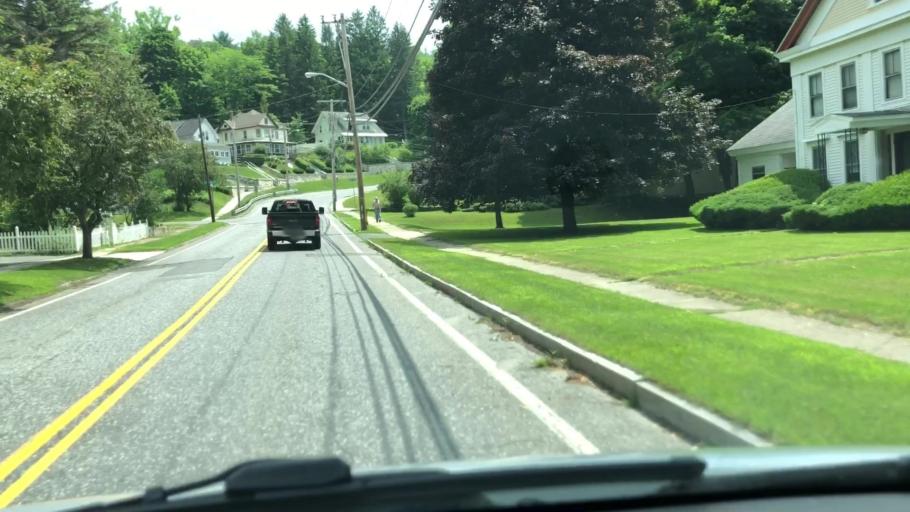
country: US
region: Massachusetts
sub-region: Berkshire County
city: Adams
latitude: 42.6179
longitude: -73.1175
